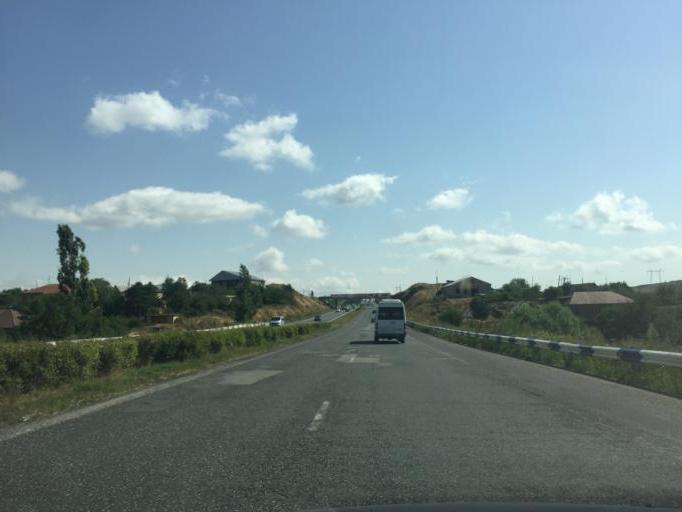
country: AM
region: Kotayk'i Marz
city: Hrazdan
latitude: 40.4896
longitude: 44.7739
